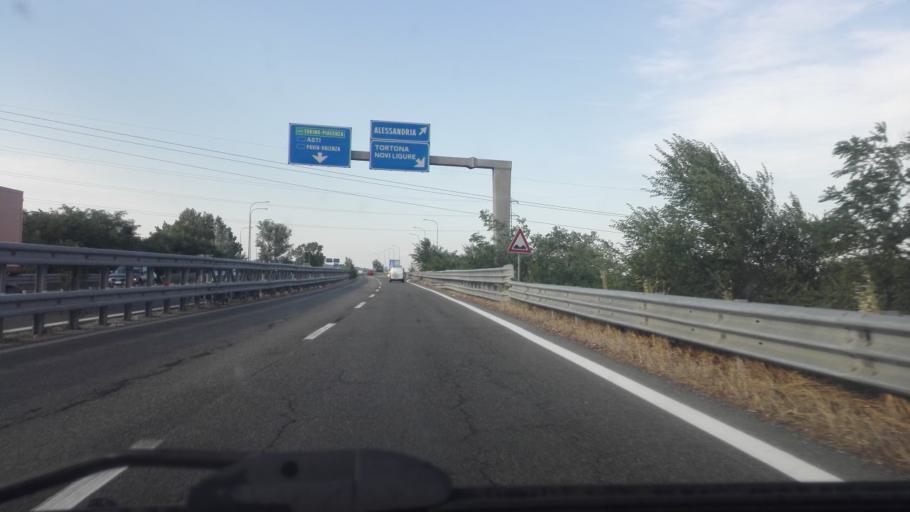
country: IT
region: Piedmont
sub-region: Provincia di Alessandria
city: Alessandria
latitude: 44.9040
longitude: 8.6385
